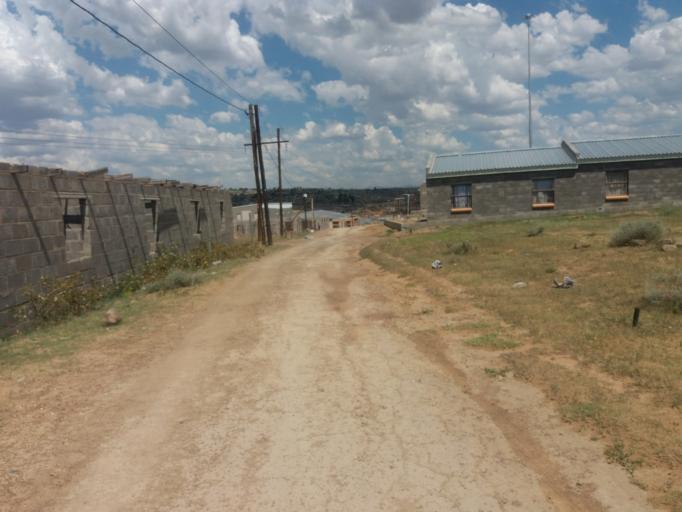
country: LS
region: Maseru
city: Maseru
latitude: -29.3664
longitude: 27.4786
